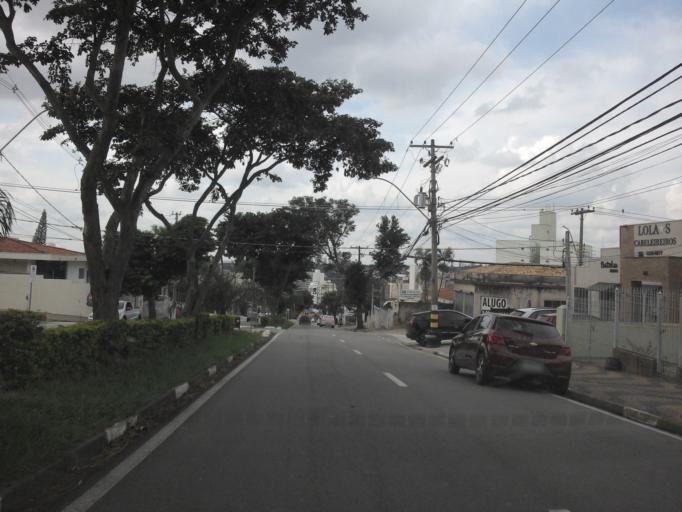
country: BR
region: Sao Paulo
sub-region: Campinas
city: Campinas
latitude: -22.9168
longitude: -47.0493
